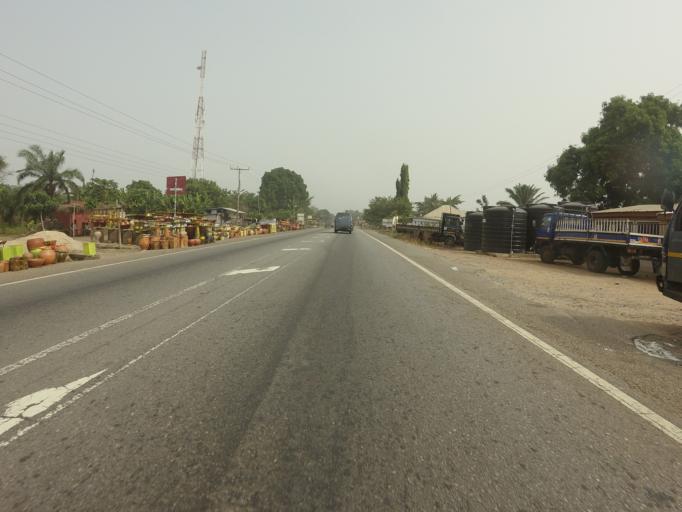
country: GH
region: Volta
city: Anloga
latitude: 6.0053
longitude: 0.5596
